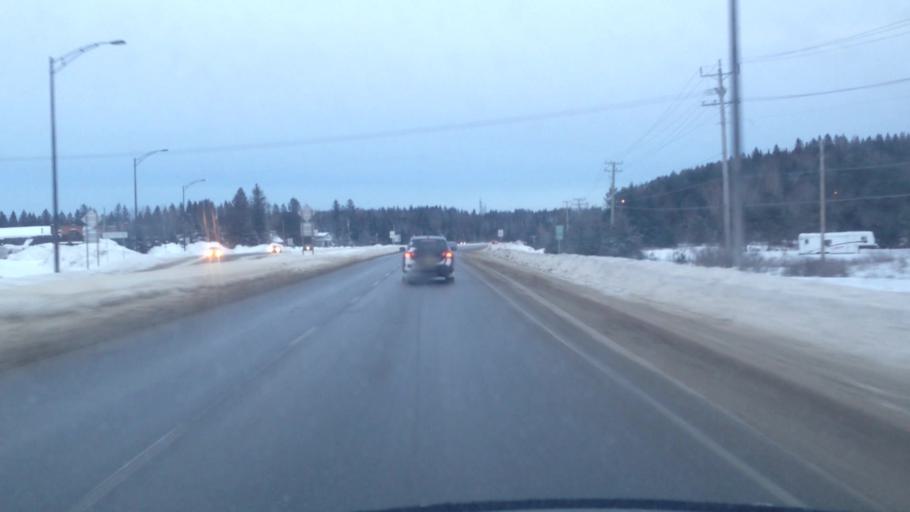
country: CA
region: Quebec
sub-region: Laurentides
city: Mont-Tremblant
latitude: 46.1169
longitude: -74.5611
